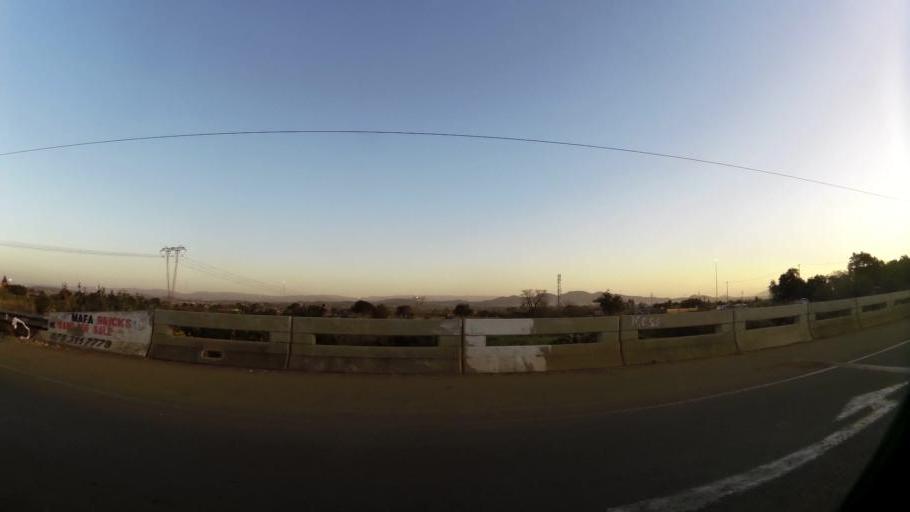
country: ZA
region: North-West
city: Ga-Rankuwa
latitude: -25.5731
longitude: 28.0643
